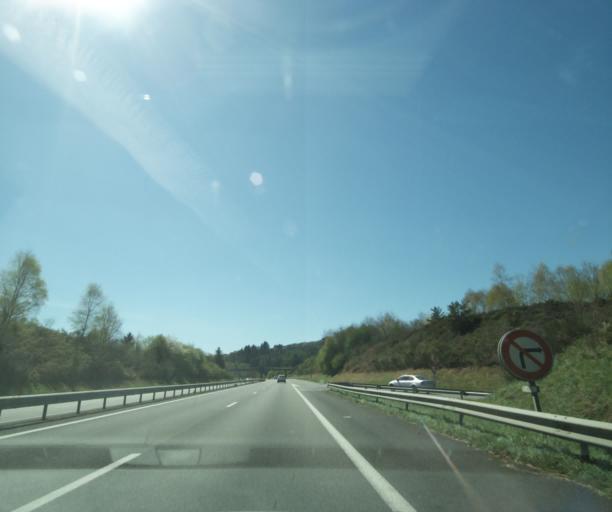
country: FR
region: Limousin
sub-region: Departement de la Haute-Vienne
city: Razes
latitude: 46.0187
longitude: 1.3404
